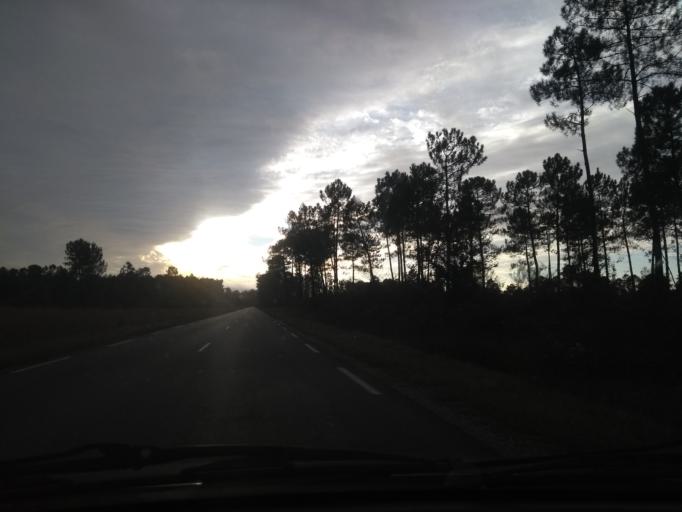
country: FR
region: Aquitaine
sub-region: Departement de la Gironde
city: Le Barp
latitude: 44.5968
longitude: -0.7125
